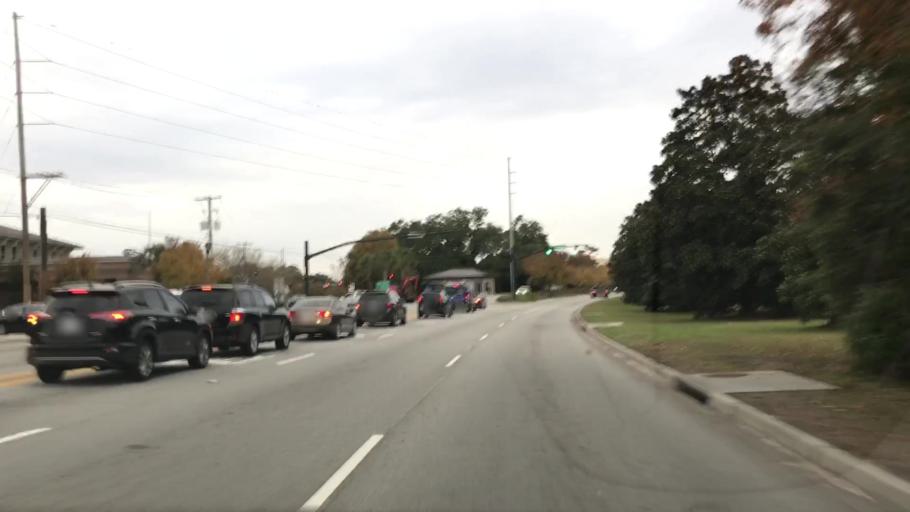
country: US
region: South Carolina
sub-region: Charleston County
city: Charleston
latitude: 32.7606
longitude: -79.9745
